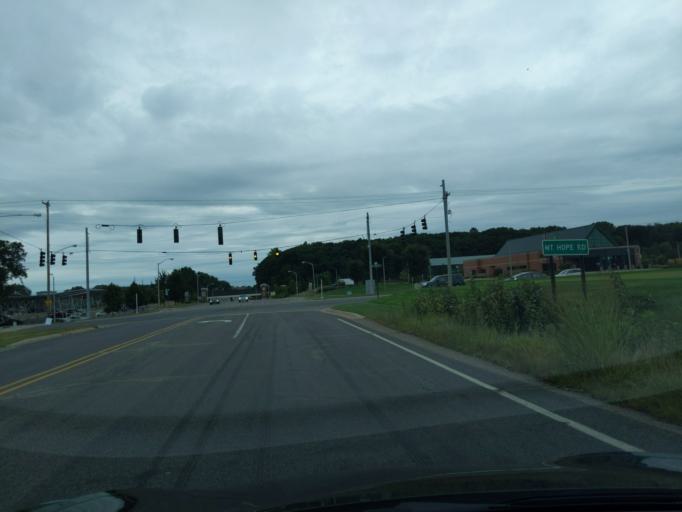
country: US
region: Michigan
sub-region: Ingham County
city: East Lansing
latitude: 42.7113
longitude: -84.4782
